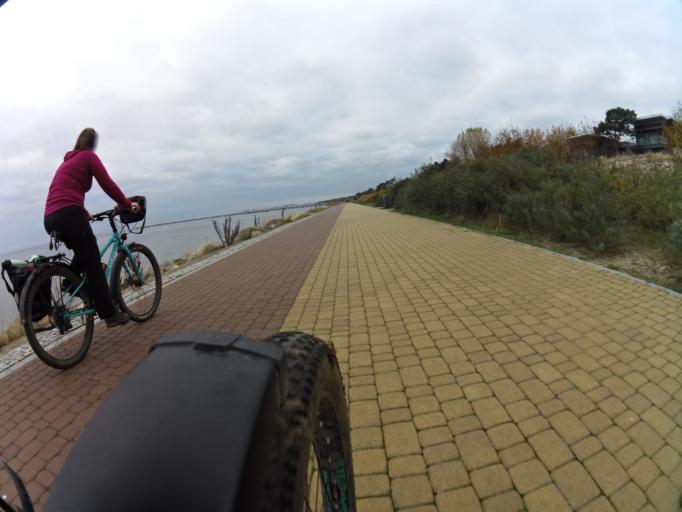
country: PL
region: Pomeranian Voivodeship
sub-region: Powiat pucki
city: Jastarnia
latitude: 54.6790
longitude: 18.7147
